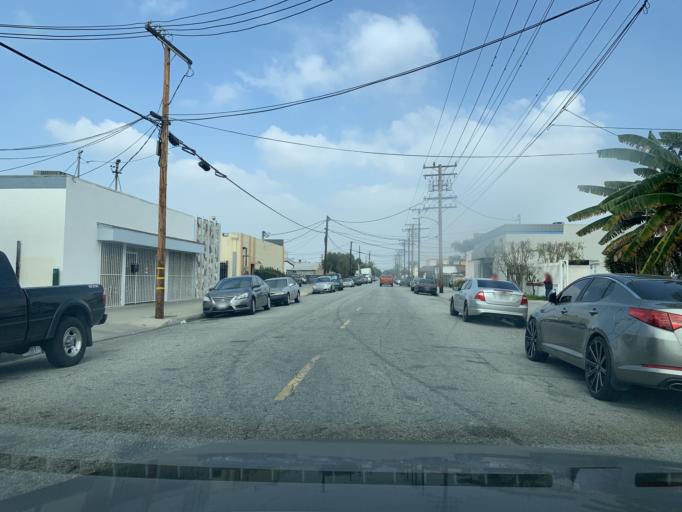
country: US
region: California
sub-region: Los Angeles County
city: South El Monte
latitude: 34.0528
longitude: -118.0528
